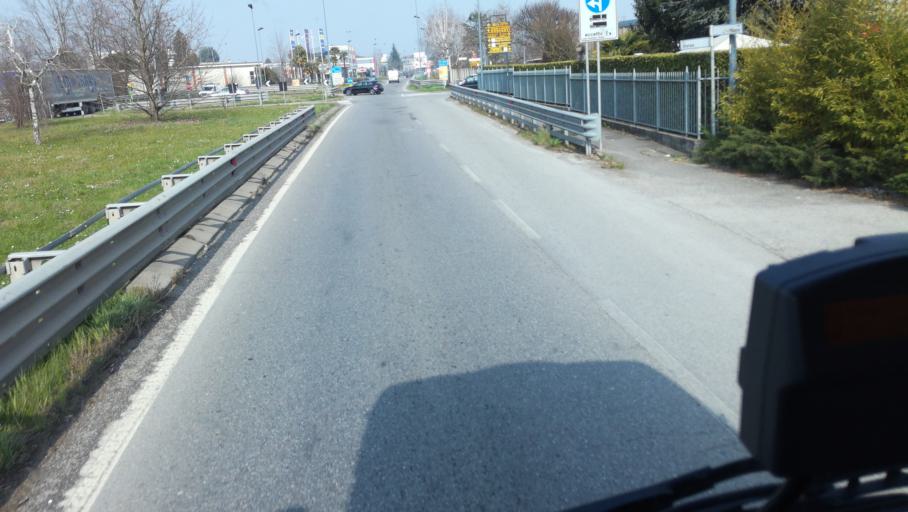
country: IT
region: Lombardy
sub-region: Provincia di Lecco
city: Osnago
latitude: 45.6715
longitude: 9.3908
